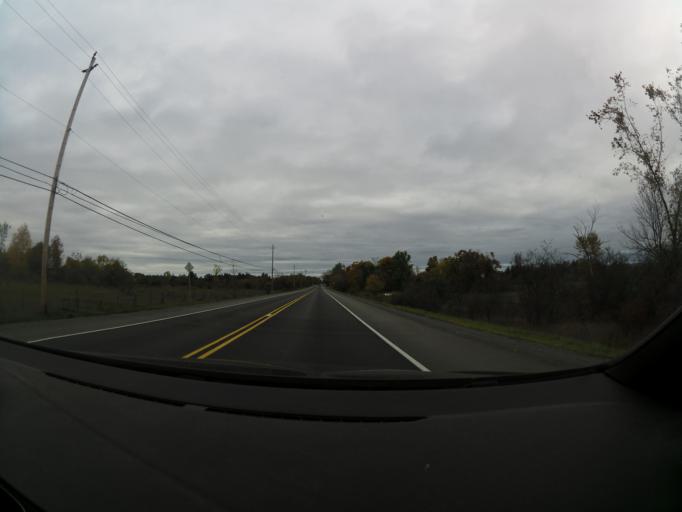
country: CA
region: Ontario
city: Bells Corners
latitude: 45.3920
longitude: -75.9826
